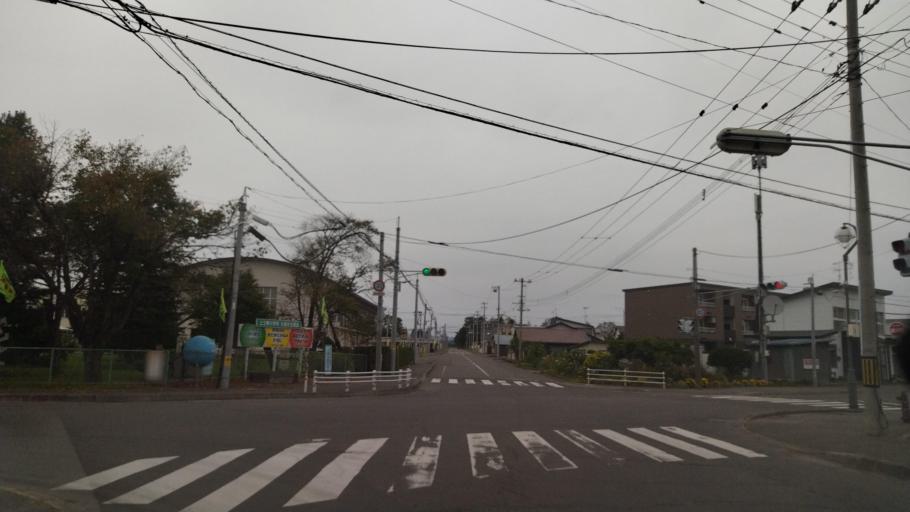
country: JP
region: Hokkaido
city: Otofuke
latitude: 43.2299
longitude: 143.2804
